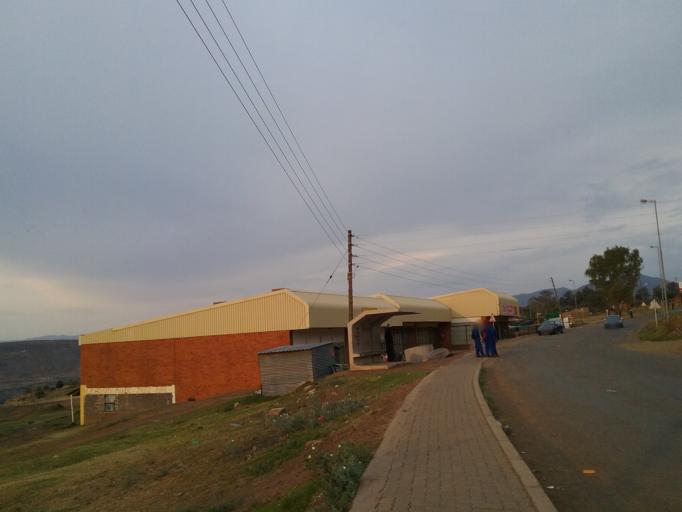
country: LS
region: Quthing
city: Quthing
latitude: -30.4084
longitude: 27.7012
